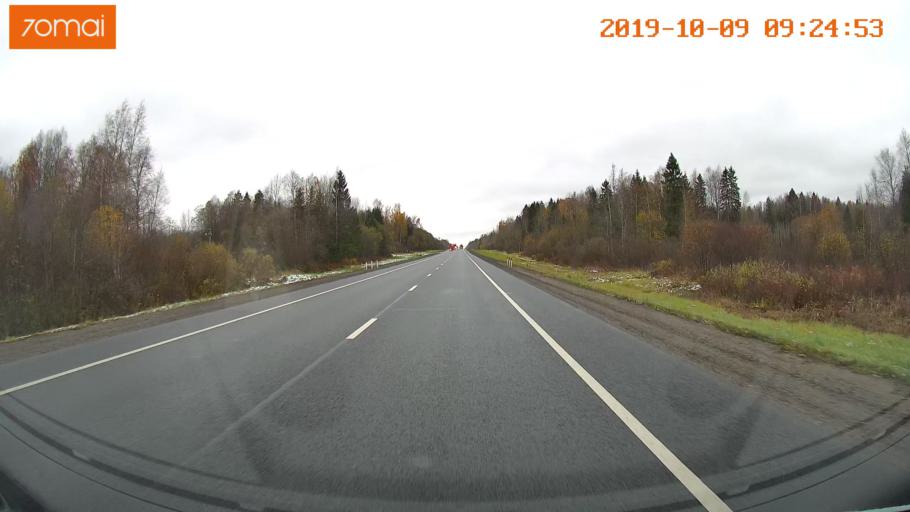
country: RU
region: Vologda
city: Vologda
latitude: 59.0840
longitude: 40.0101
